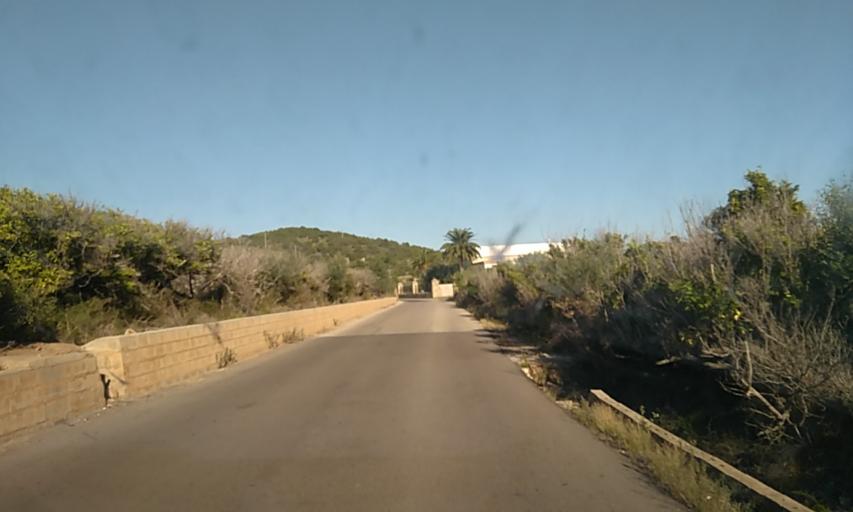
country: ES
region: Valencia
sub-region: Provincia de Castello
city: Alcoceber
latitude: 40.2488
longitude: 0.2440
